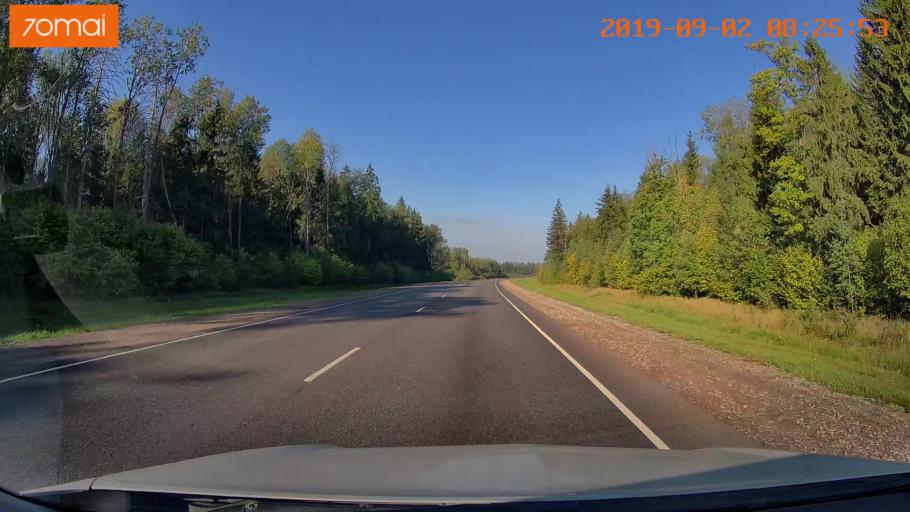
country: RU
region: Kaluga
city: Maloyaroslavets
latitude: 54.9784
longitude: 36.4522
